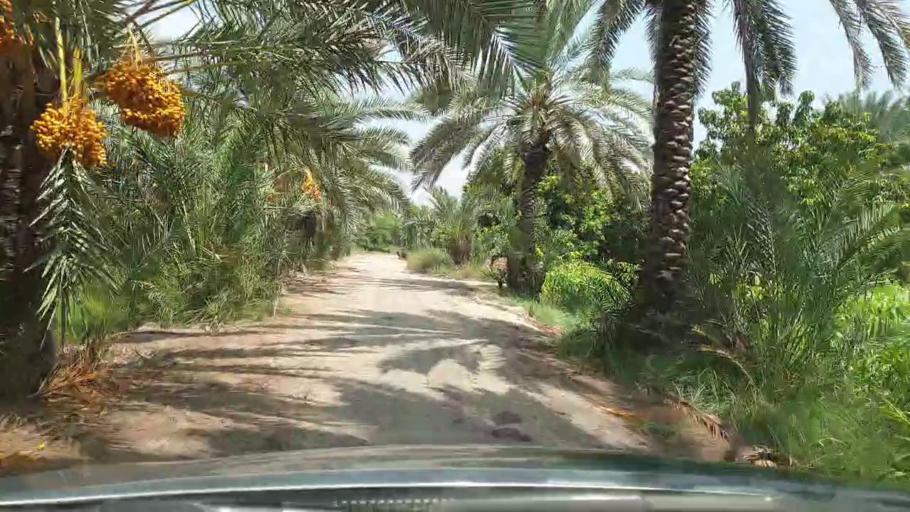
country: PK
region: Sindh
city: Pir jo Goth
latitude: 27.6227
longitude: 68.6654
